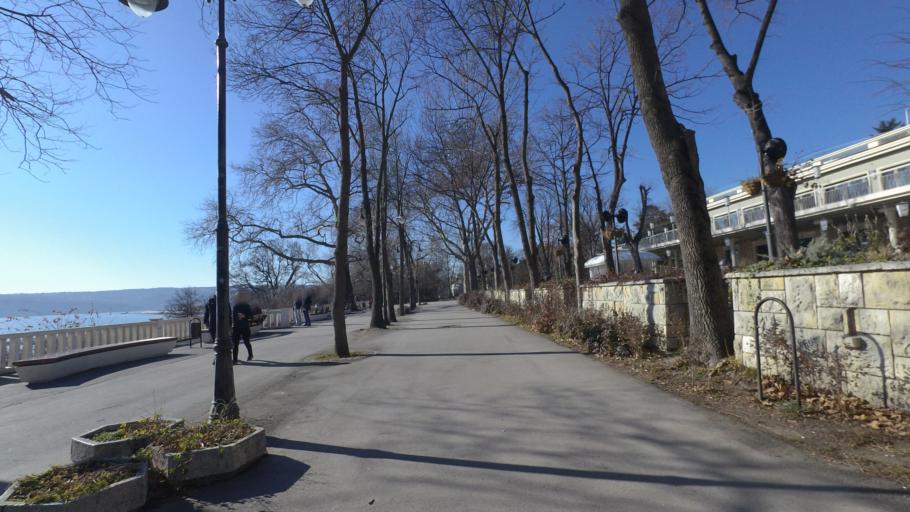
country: BG
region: Varna
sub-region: Obshtina Varna
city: Varna
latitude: 43.2037
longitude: 27.9244
